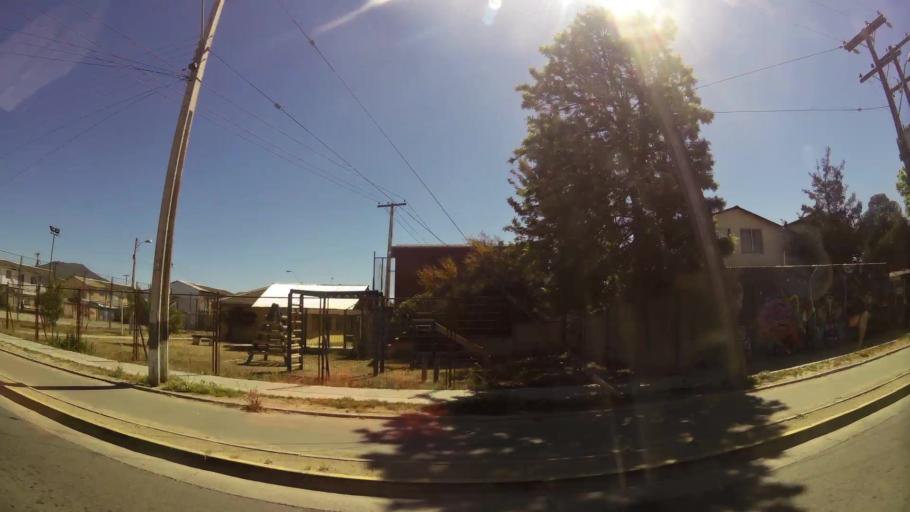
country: CL
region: Valparaiso
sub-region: Provincia de Marga Marga
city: Quilpue
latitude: -33.3070
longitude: -71.4133
